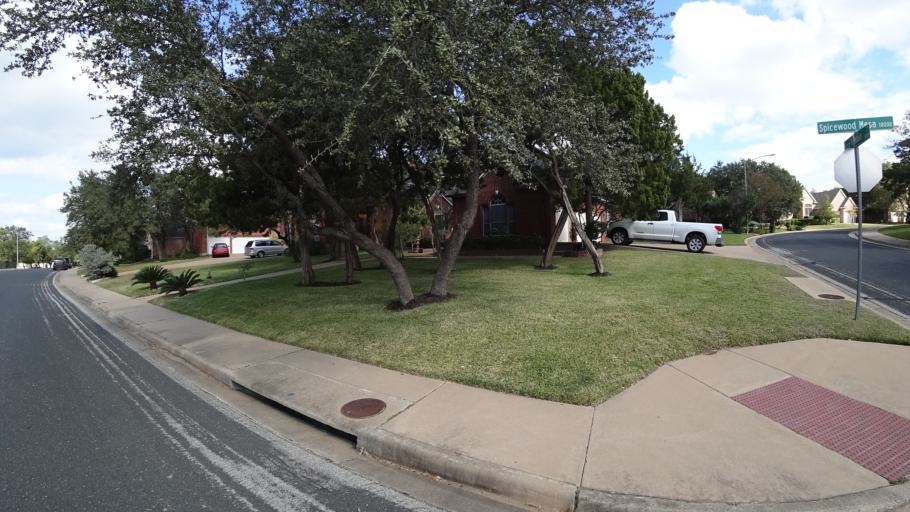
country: US
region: Texas
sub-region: Williamson County
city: Jollyville
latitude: 30.4170
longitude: -97.7912
